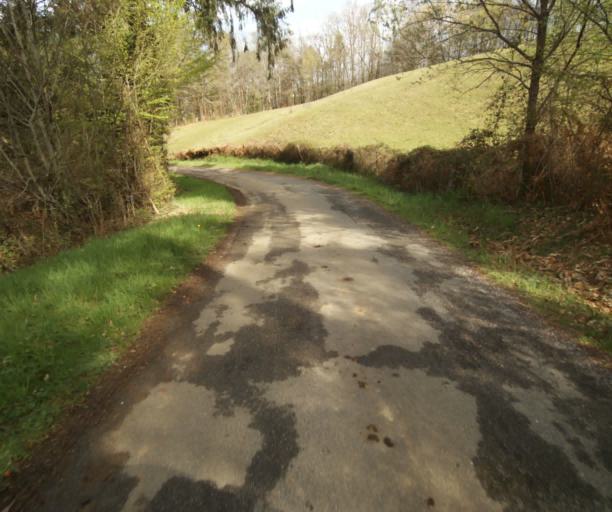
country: FR
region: Limousin
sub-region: Departement de la Correze
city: Laguenne
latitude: 45.2587
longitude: 1.8128
